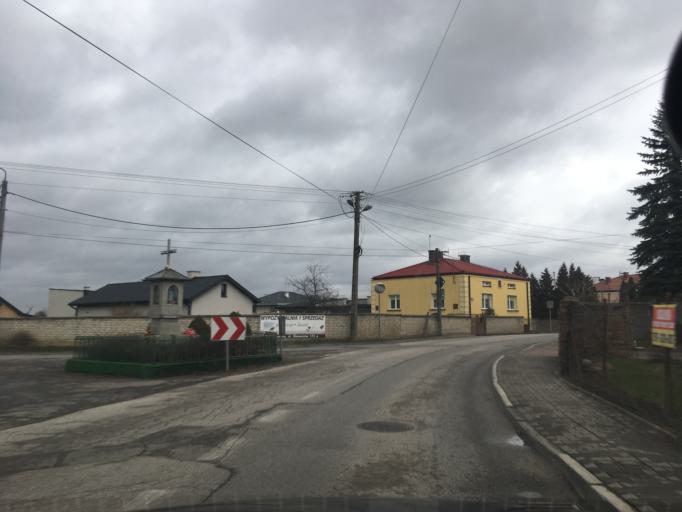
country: PL
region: Masovian Voivodeship
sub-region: Powiat pruszkowski
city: Rybie
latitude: 52.1256
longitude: 20.9553
